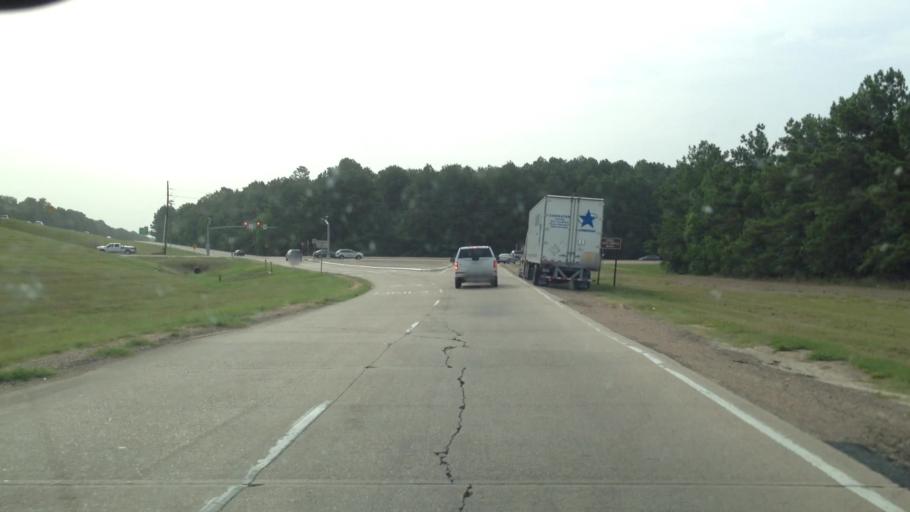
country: US
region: Louisiana
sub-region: Caddo Parish
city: Shreveport
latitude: 32.4168
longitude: -93.8166
